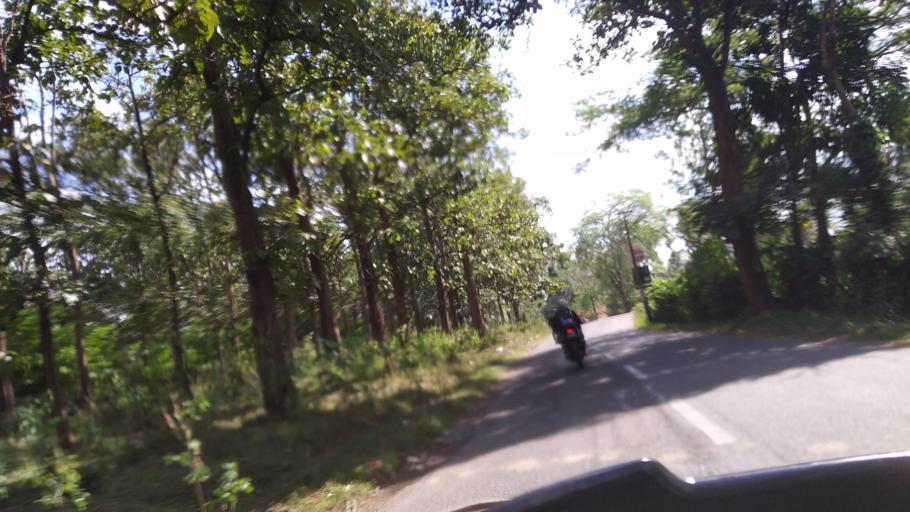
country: IN
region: Kerala
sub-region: Wayanad
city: Panamaram
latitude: 11.9397
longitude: 76.0643
